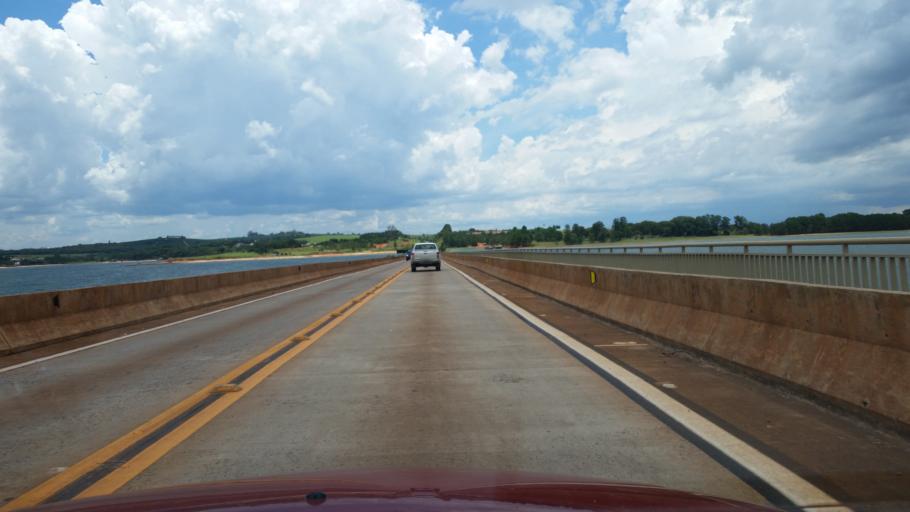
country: BR
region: Sao Paulo
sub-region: Itai
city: Itai
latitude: -23.2677
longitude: -49.0087
